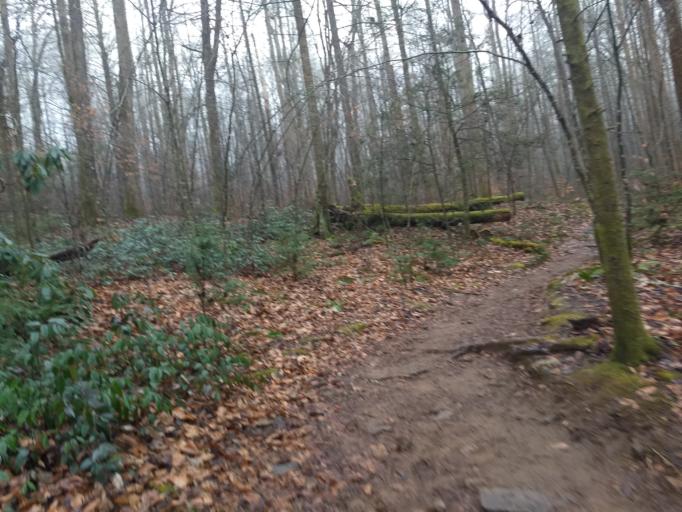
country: US
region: North Carolina
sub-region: Transylvania County
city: Brevard
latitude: 35.2755
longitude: -82.7820
